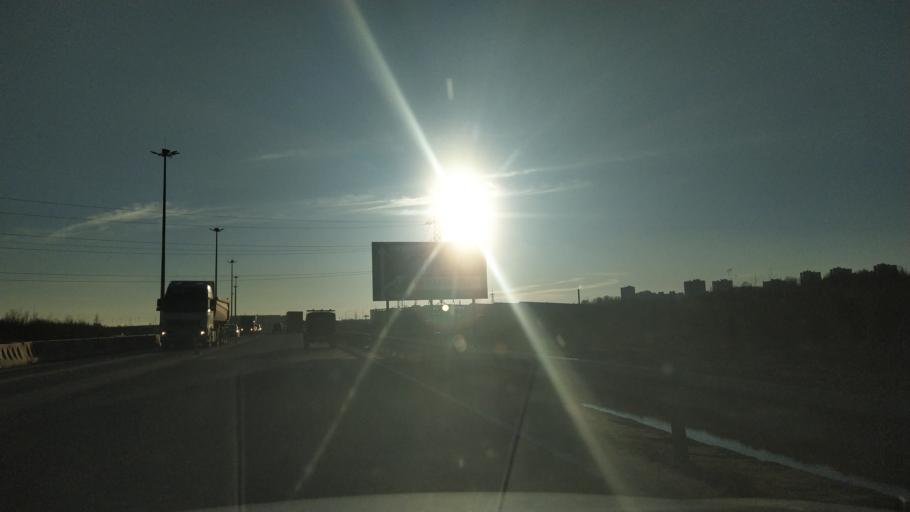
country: RU
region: St.-Petersburg
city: Pargolovo
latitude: 60.0994
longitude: 30.2851
